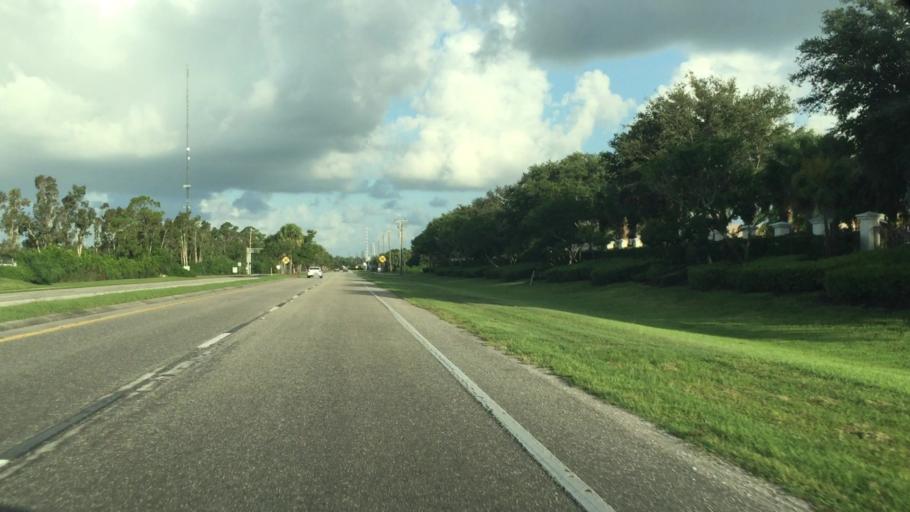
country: US
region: Florida
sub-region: Lee County
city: Estero
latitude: 26.4493
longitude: -81.8082
